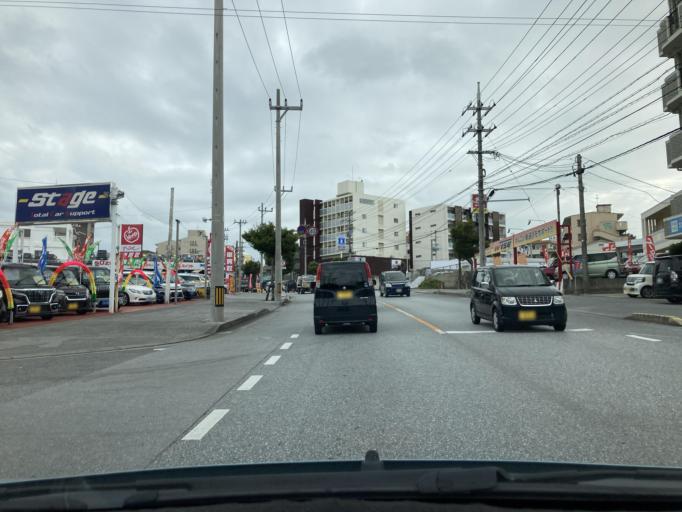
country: JP
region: Okinawa
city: Ginowan
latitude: 26.2434
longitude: 127.7644
